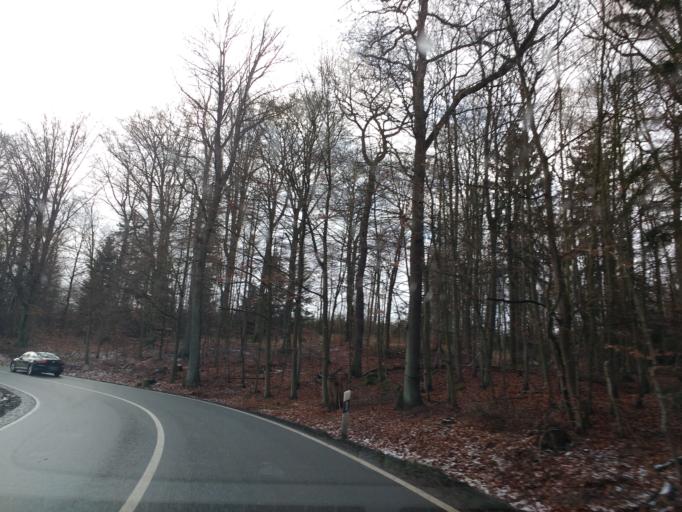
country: DE
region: Saxony-Anhalt
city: Neinstedt
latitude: 51.7121
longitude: 11.0795
